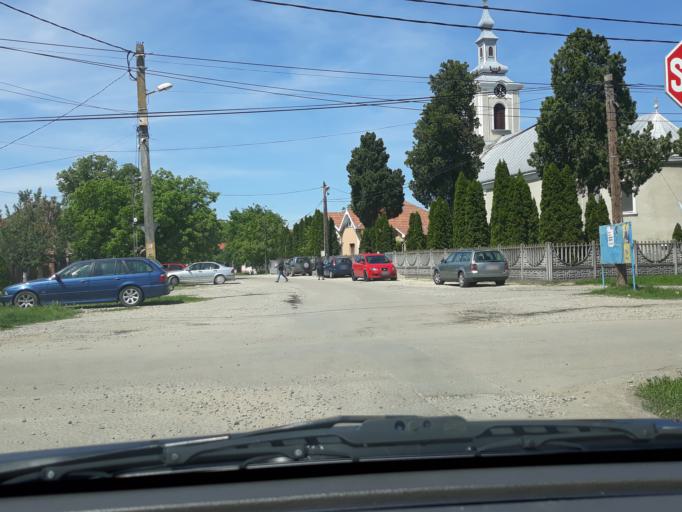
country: RO
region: Bihor
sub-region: Comuna Santandrei
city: Santandrei
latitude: 47.0690
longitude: 21.8533
